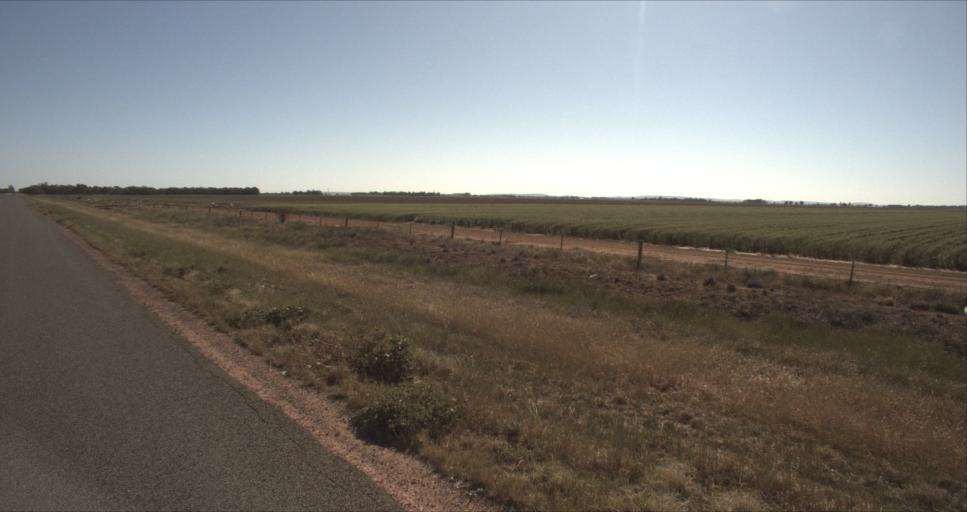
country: AU
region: New South Wales
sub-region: Leeton
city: Leeton
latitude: -34.5733
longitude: 146.2630
